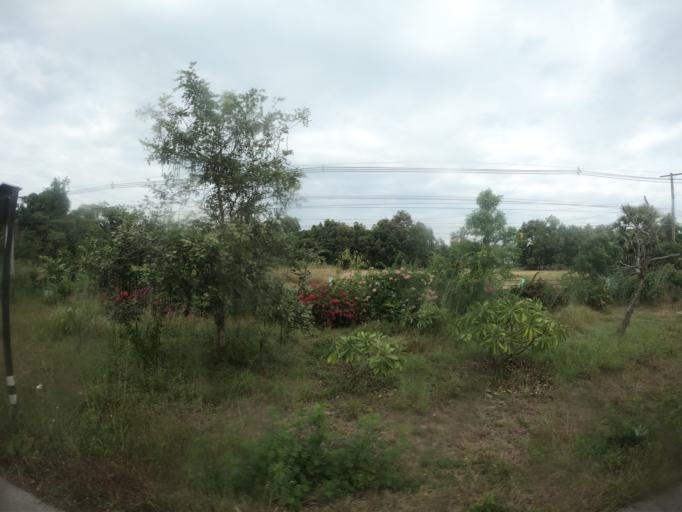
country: TH
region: Maha Sarakham
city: Kantharawichai
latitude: 16.3386
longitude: 103.2129
